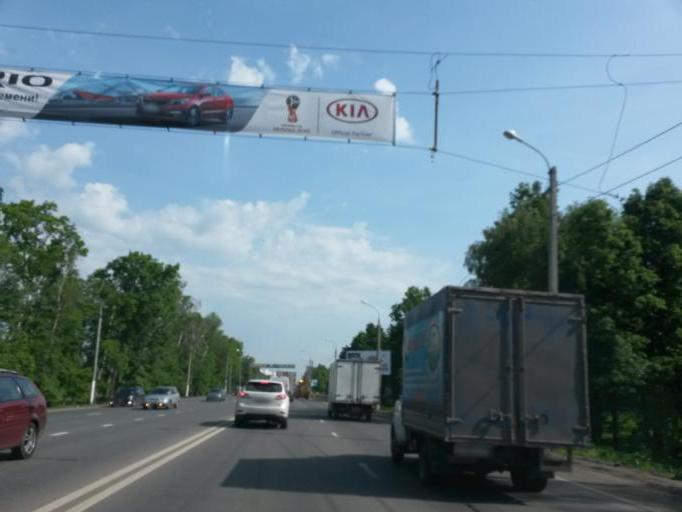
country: RU
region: Moskovskaya
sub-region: Chekhovskiy Rayon
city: Chekhov
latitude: 55.1576
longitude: 37.4641
